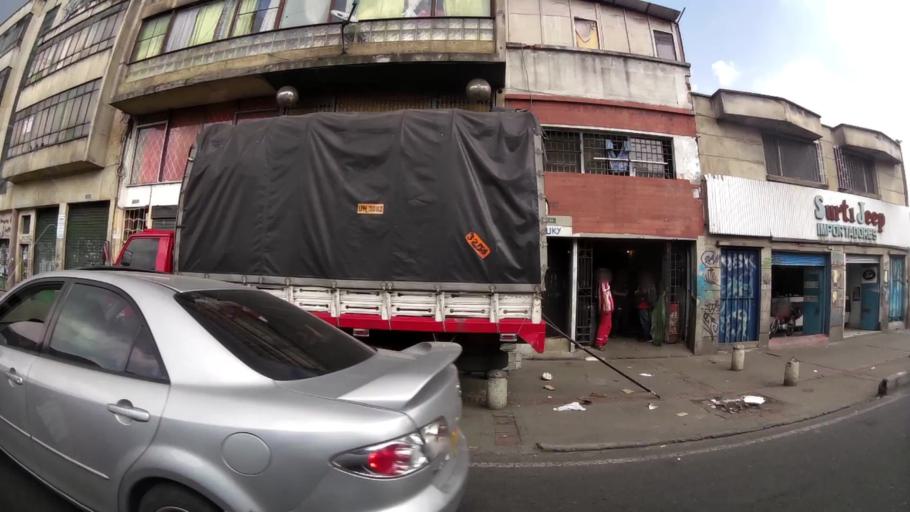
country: CO
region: Bogota D.C.
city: Bogota
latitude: 4.6104
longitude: -74.0752
